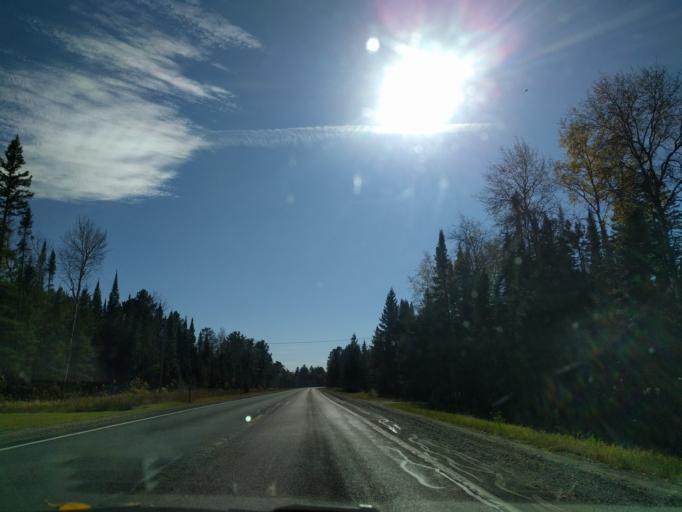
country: US
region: Michigan
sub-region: Marquette County
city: West Ishpeming
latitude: 46.3222
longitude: -87.9698
